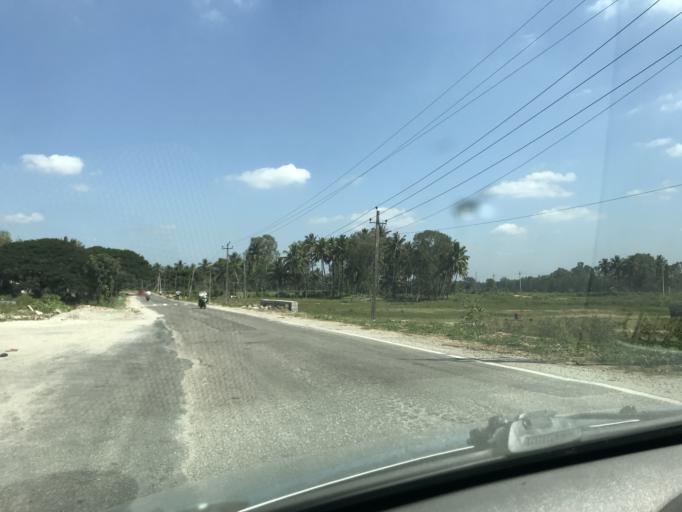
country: IN
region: Karnataka
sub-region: Mysore
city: Hunsur
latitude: 12.3483
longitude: 76.2892
